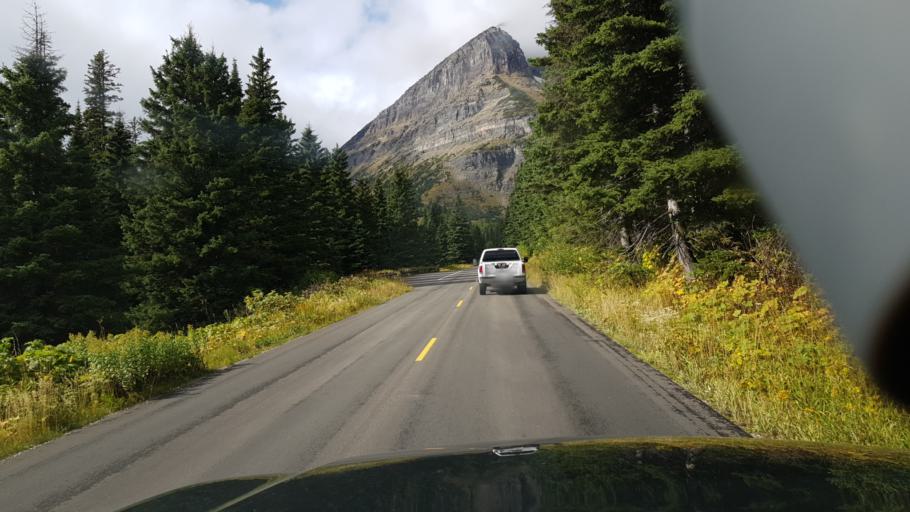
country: US
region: Montana
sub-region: Flathead County
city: Columbia Falls
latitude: 48.6846
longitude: -113.6631
